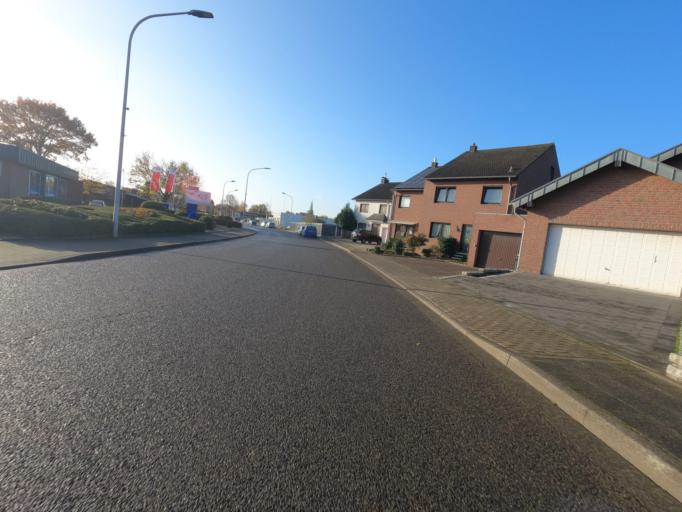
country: DE
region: North Rhine-Westphalia
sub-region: Regierungsbezirk Koln
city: Heinsberg
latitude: 51.0665
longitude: 6.1029
